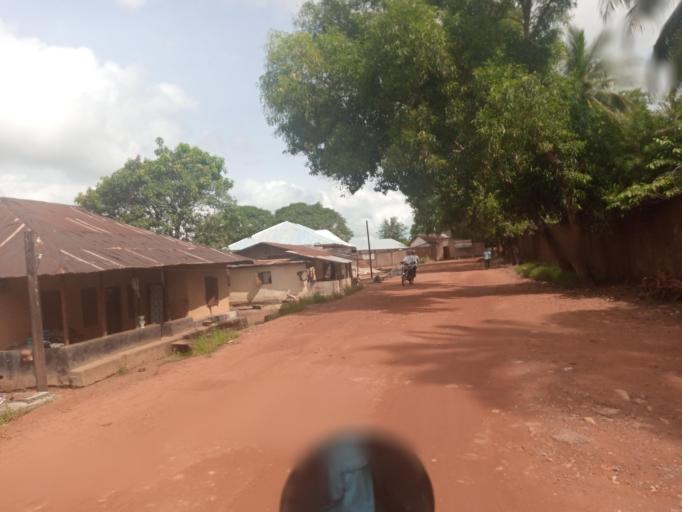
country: SL
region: Southern Province
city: Bo
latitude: 7.9678
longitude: -11.7423
